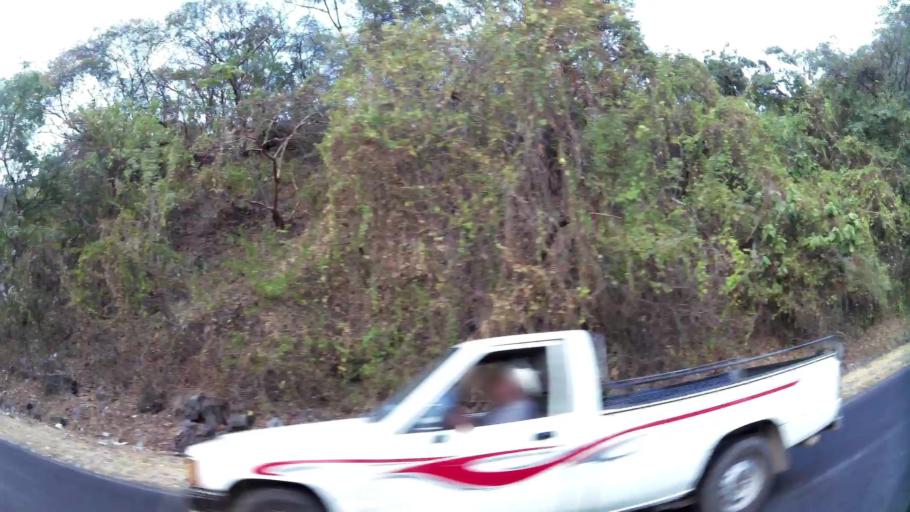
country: SV
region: San Vicente
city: Apastepeque
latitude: 13.6541
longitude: -88.7875
